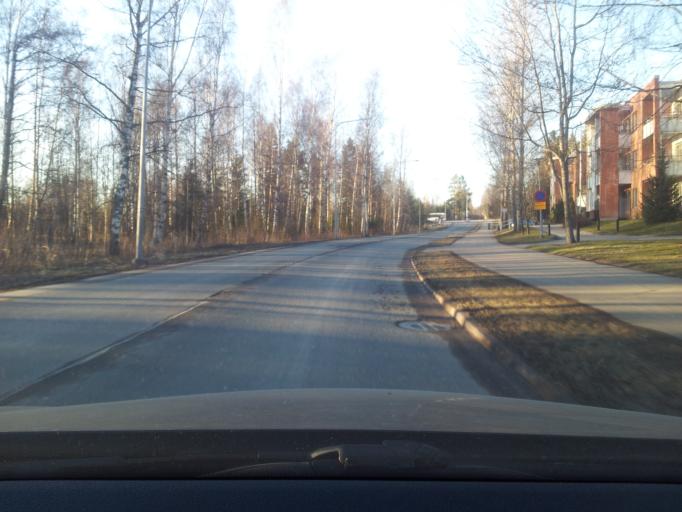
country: FI
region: Uusimaa
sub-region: Helsinki
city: Koukkuniemi
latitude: 60.1596
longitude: 24.7622
